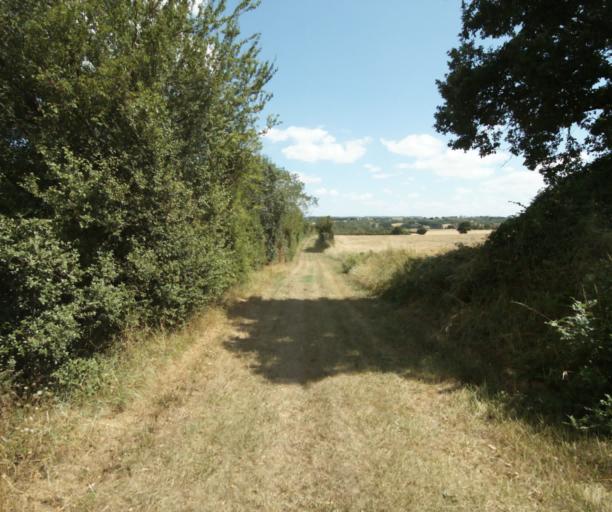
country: FR
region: Midi-Pyrenees
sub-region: Departement de la Haute-Garonne
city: Auriac-sur-Vendinelle
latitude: 43.4732
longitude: 1.8372
